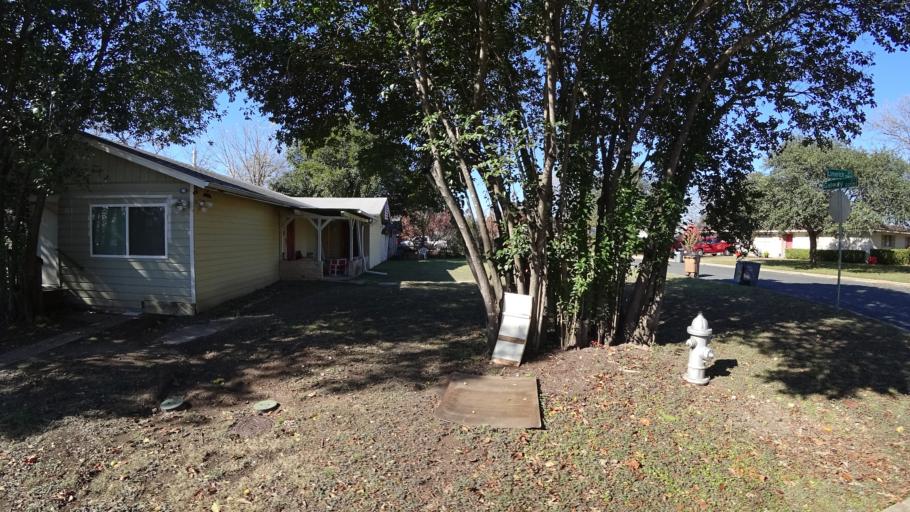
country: US
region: Texas
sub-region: Travis County
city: Wells Branch
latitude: 30.4158
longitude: -97.6990
